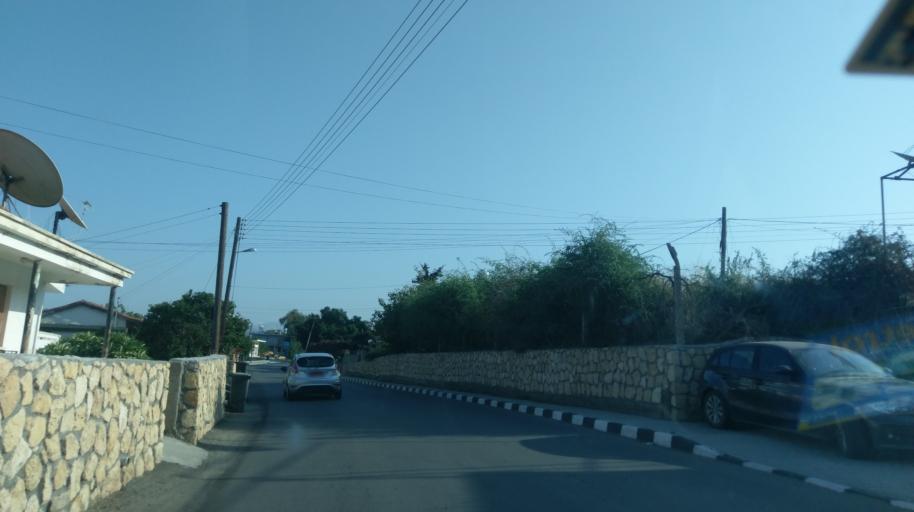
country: CY
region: Lefkosia
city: Lefka
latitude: 35.1452
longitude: 32.8061
